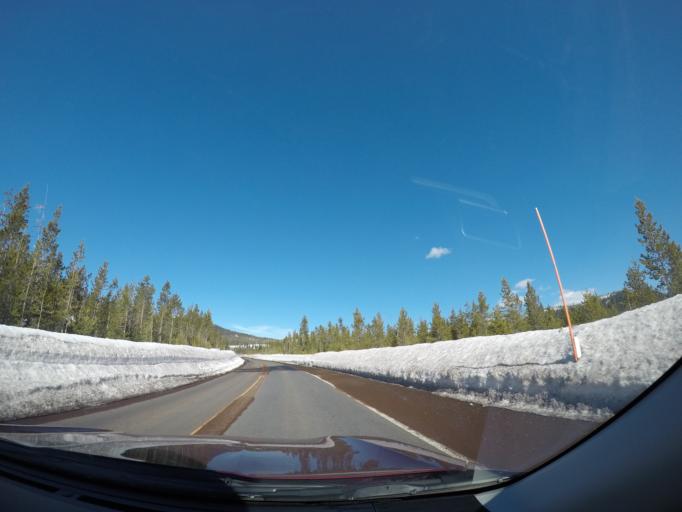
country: US
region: Oregon
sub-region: Deschutes County
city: Sunriver
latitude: 43.9766
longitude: -121.6101
